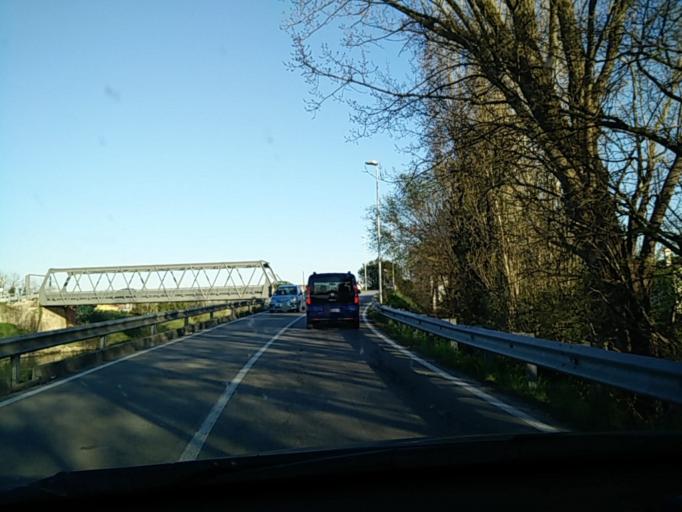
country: IT
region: Veneto
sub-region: Provincia di Venezia
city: Quarto d'Altino
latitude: 45.5815
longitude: 12.3729
